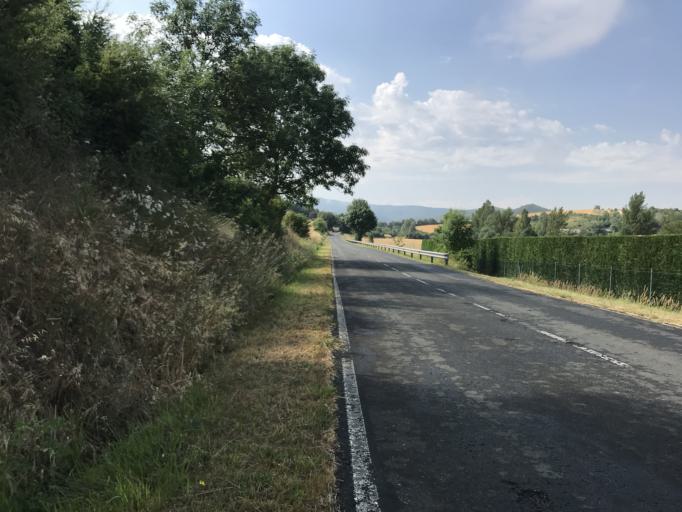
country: ES
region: Basque Country
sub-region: Provincia de Alava
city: Gasteiz / Vitoria
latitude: 42.8209
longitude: -2.6473
